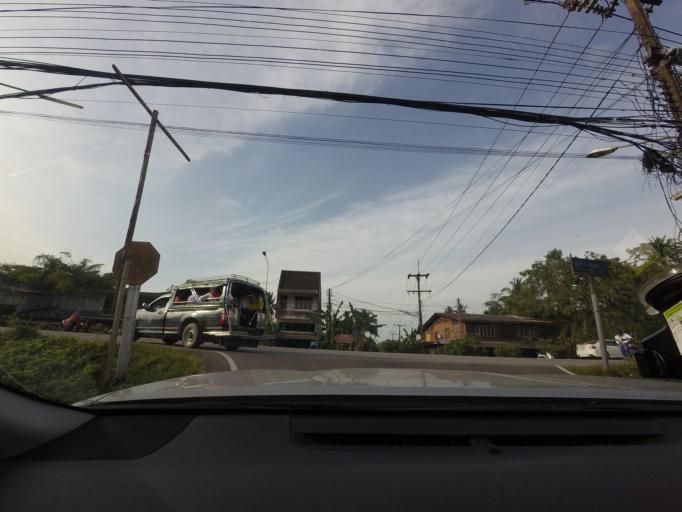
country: TH
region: Narathiwat
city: Ra-ngae
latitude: 6.2980
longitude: 101.7337
